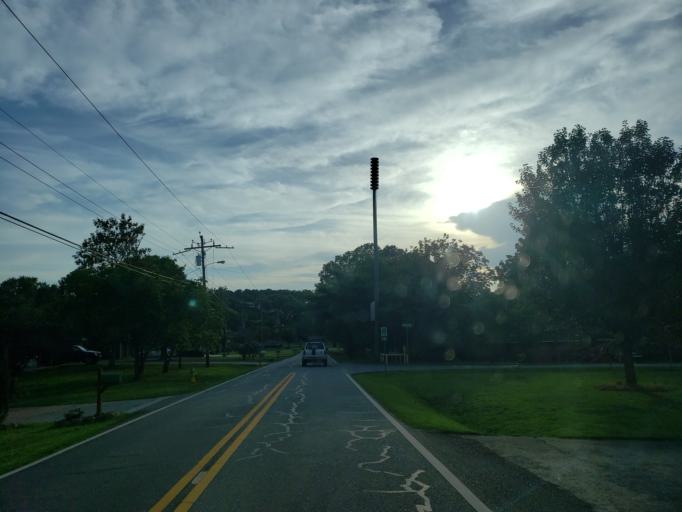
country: US
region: Georgia
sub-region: Bartow County
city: Cartersville
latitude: 34.1969
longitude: -84.8164
